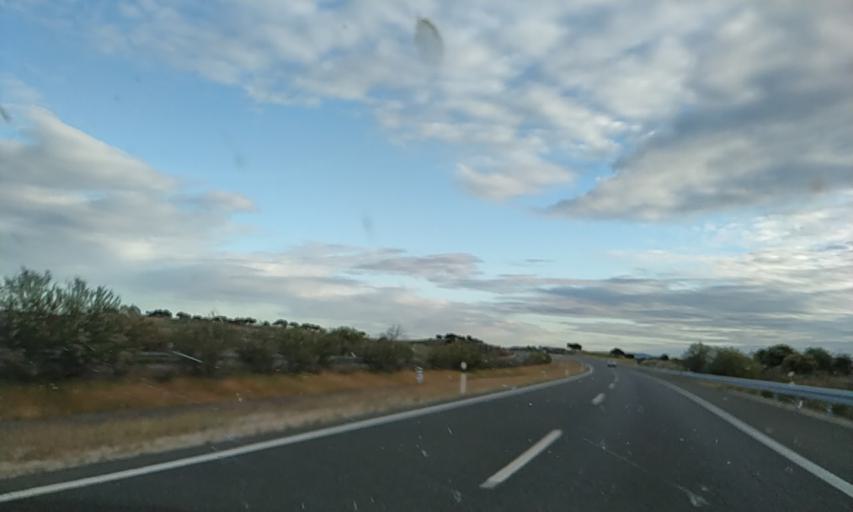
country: ES
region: Extremadura
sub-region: Provincia de Caceres
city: Casar de Caceres
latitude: 39.5027
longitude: -6.4378
